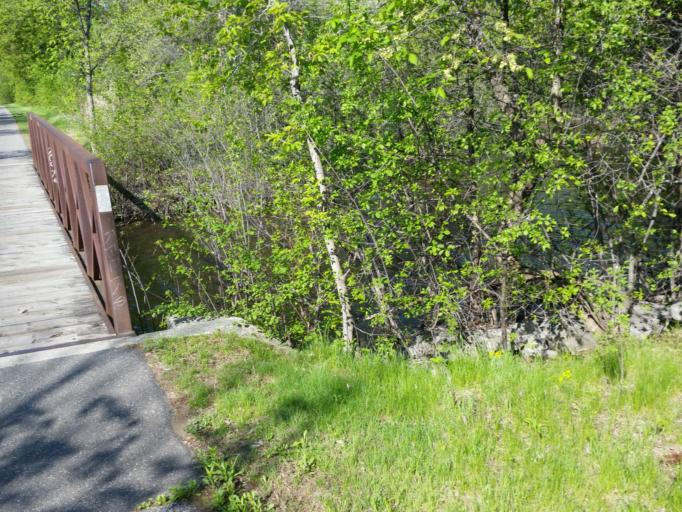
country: CA
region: Ontario
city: Ottawa
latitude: 45.4174
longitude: -75.7561
